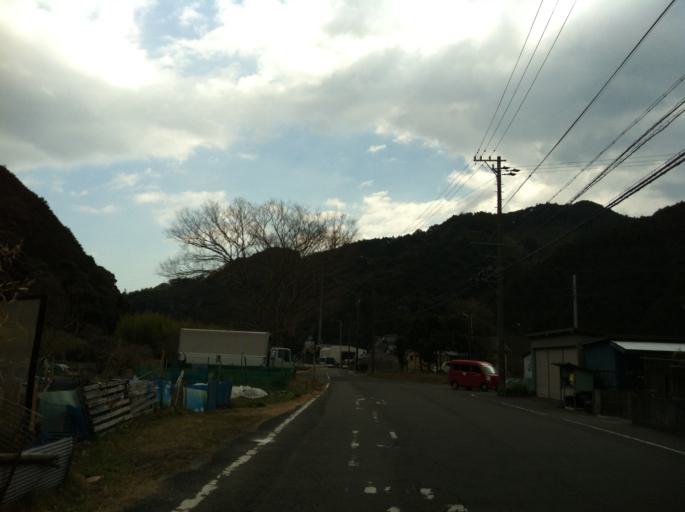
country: JP
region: Shizuoka
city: Shizuoka-shi
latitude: 35.0554
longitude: 138.3422
